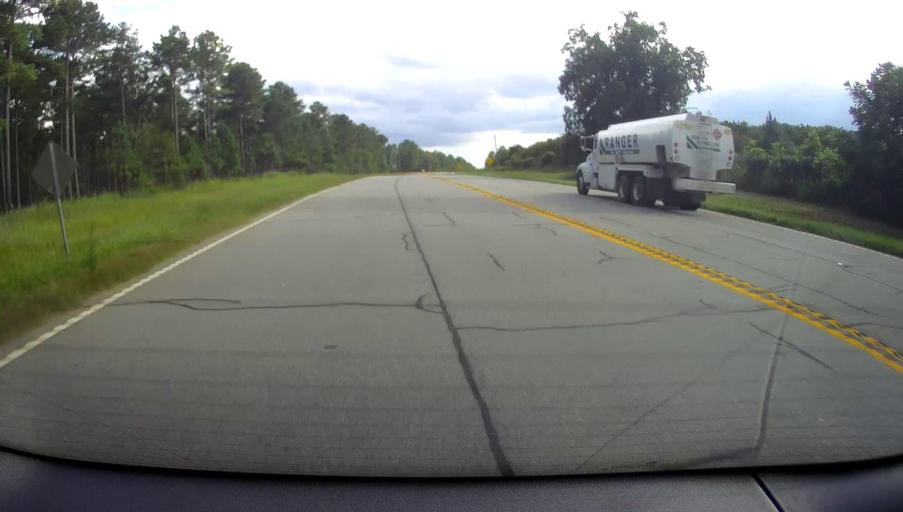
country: US
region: Georgia
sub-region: Meriwether County
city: Greenville
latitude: 33.0110
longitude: -84.5661
